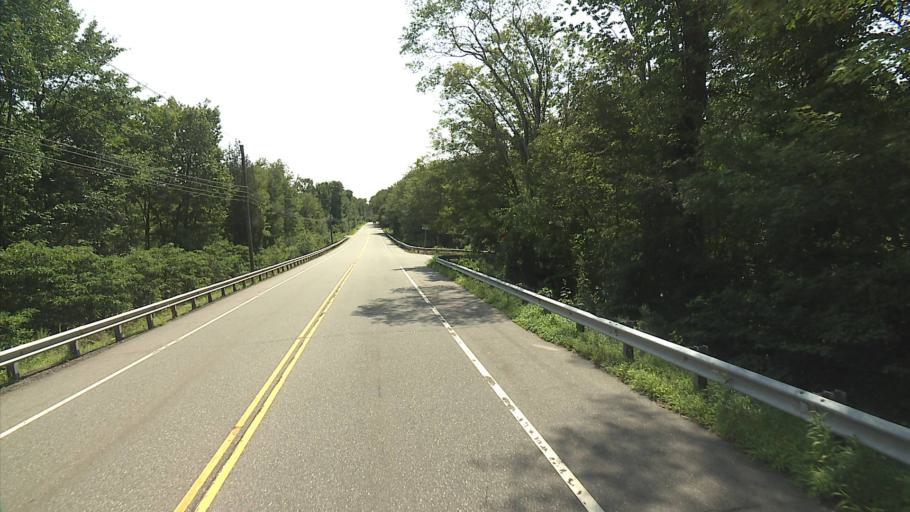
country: US
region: Connecticut
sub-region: New London County
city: Colchester
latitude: 41.5560
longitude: -72.2922
